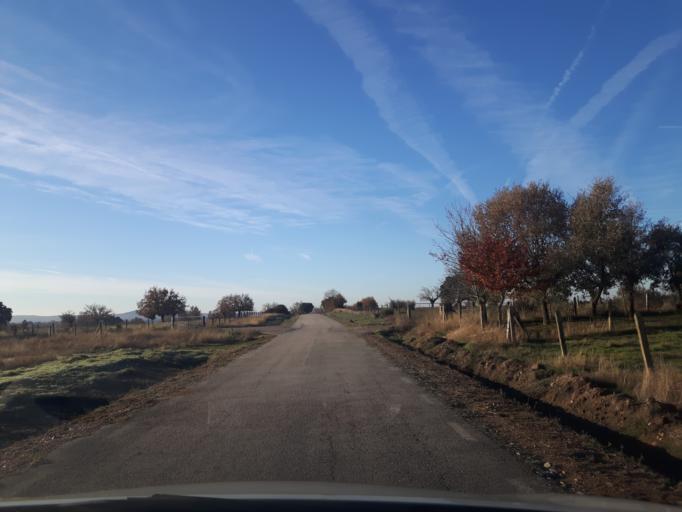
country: ES
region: Castille and Leon
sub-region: Provincia de Salamanca
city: Cerralbo
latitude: 40.9609
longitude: -6.5955
